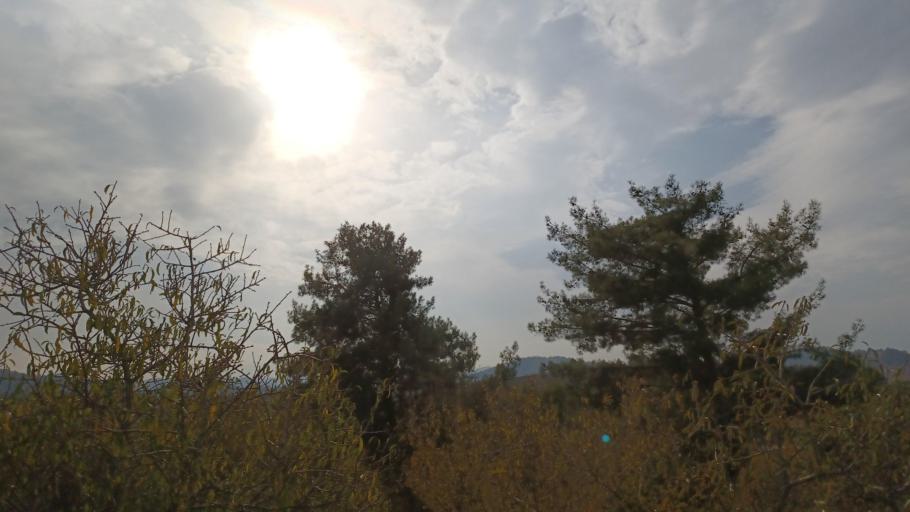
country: CY
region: Lefkosia
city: Klirou
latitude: 35.0348
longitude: 33.1352
